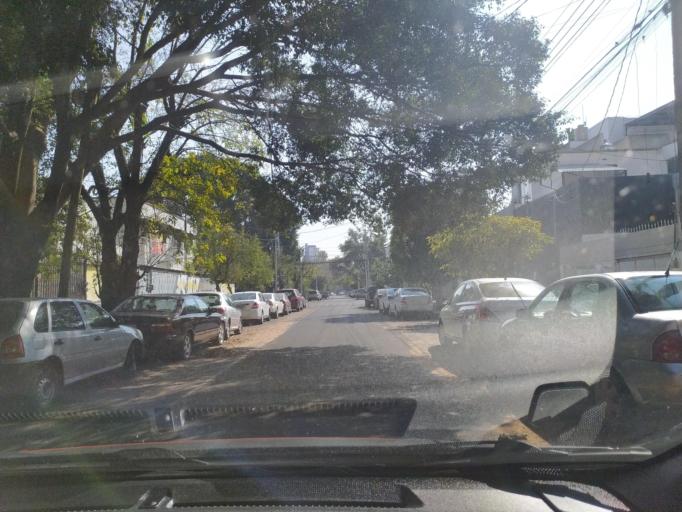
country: MX
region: Jalisco
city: Guadalajara
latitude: 20.6759
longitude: -103.3760
